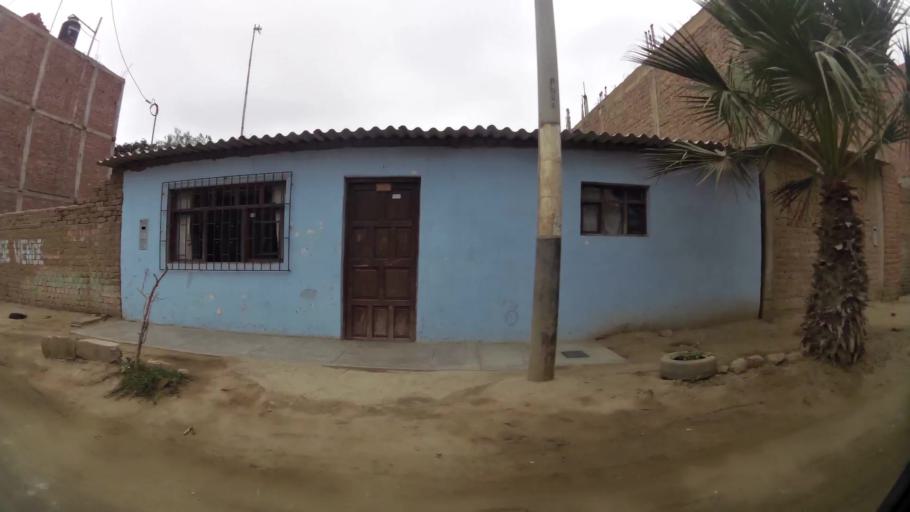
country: PE
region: La Libertad
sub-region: Provincia de Trujillo
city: La Esperanza
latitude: -8.0897
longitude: -79.0441
